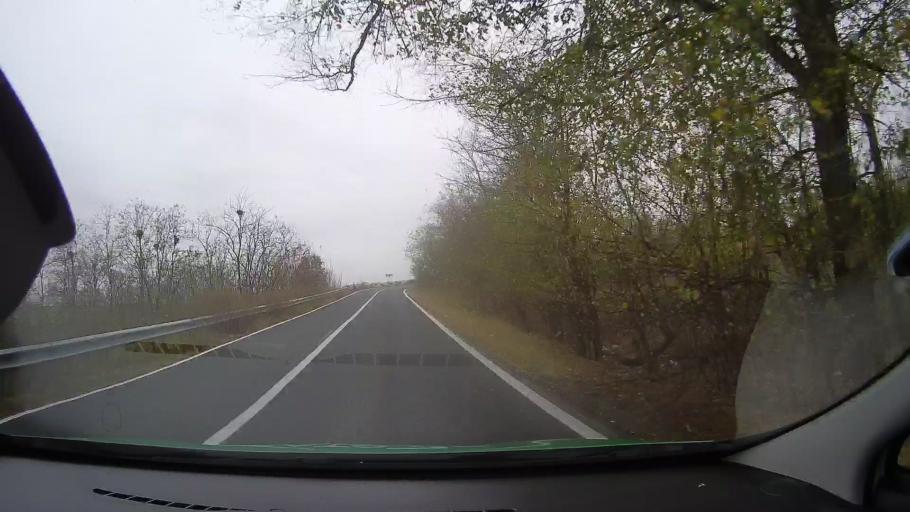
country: RO
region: Constanta
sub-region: Comuna Saraiu
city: Saraiu
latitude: 44.7124
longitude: 28.1241
